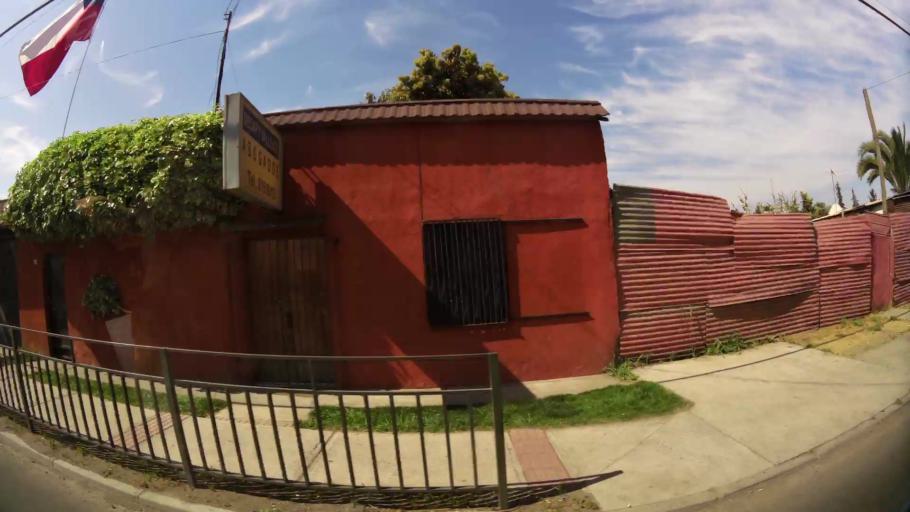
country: CL
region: Santiago Metropolitan
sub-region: Provincia de Talagante
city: Talagante
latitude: -33.6693
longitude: -70.9384
